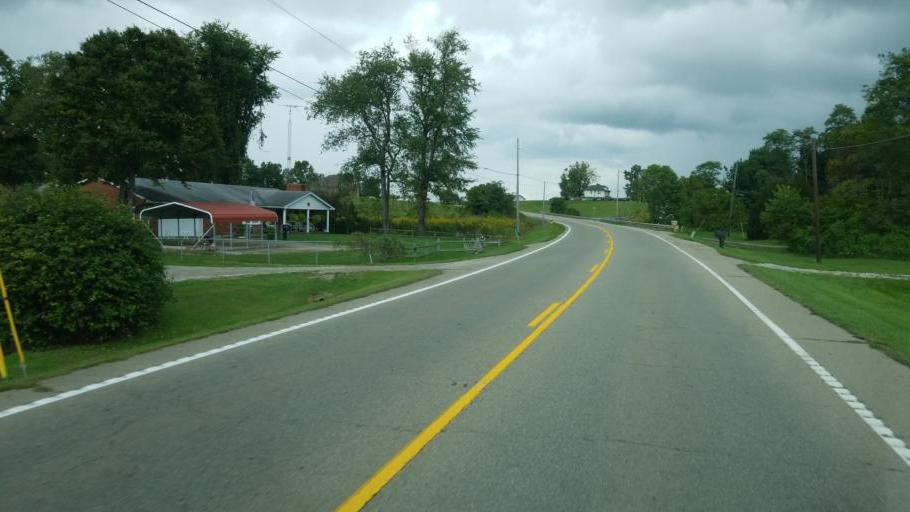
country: US
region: Ohio
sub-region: Jackson County
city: Jackson
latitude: 39.0165
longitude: -82.6050
